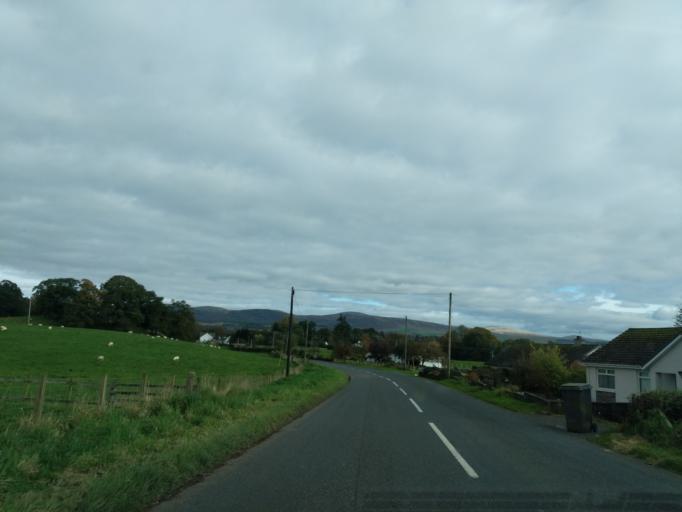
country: GB
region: Scotland
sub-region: Dumfries and Galloway
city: Thornhill
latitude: 55.2370
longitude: -3.7971
